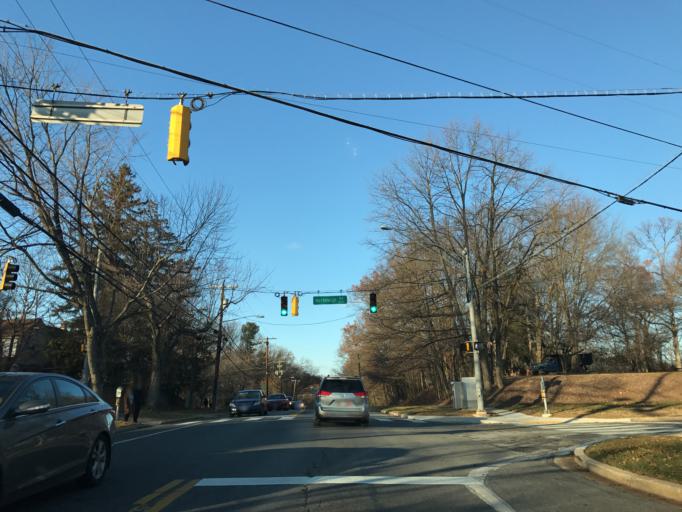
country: US
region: Maryland
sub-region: Montgomery County
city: Kemp Mill
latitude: 39.0505
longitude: -77.0248
